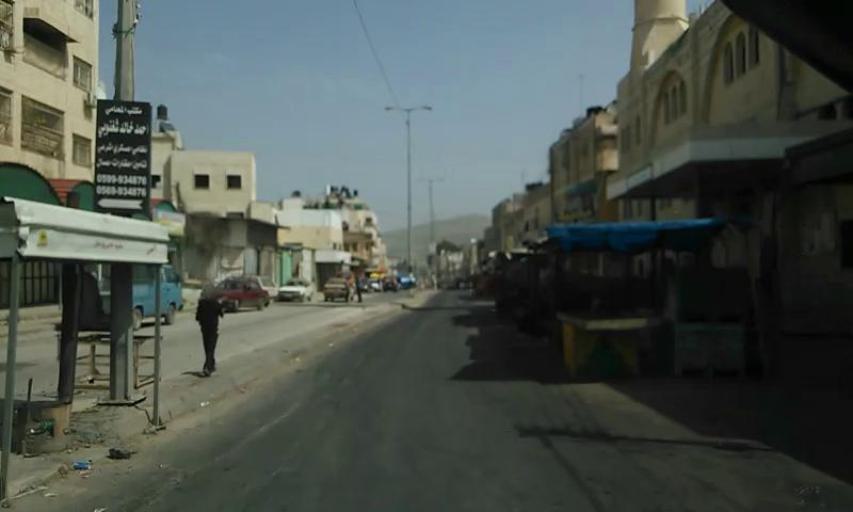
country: PS
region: West Bank
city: `Azmut
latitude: 32.2207
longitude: 35.2966
